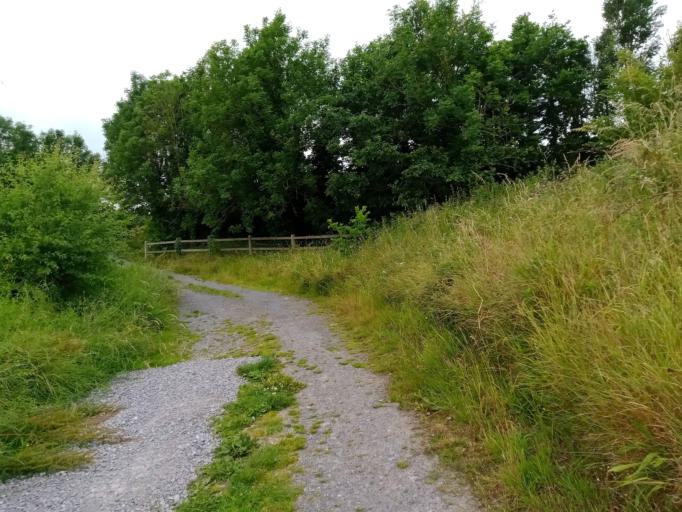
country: IE
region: Leinster
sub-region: Kilkenny
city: Callan
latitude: 52.5474
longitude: -7.3938
